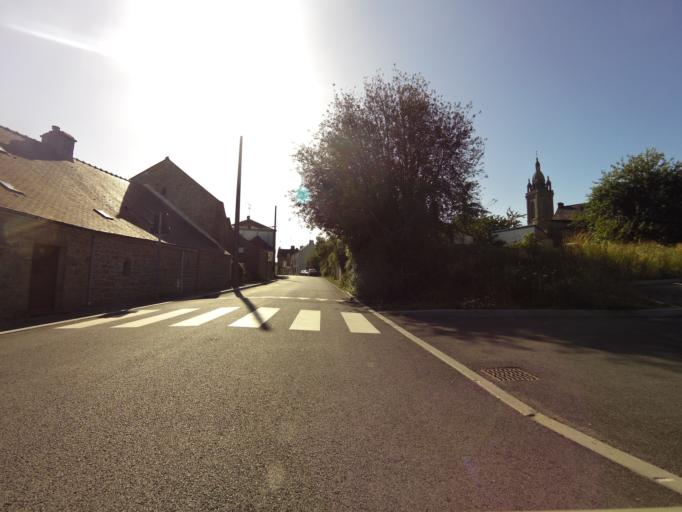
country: FR
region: Brittany
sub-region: Departement du Morbihan
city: Limerzel
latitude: 47.6350
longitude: -2.3526
